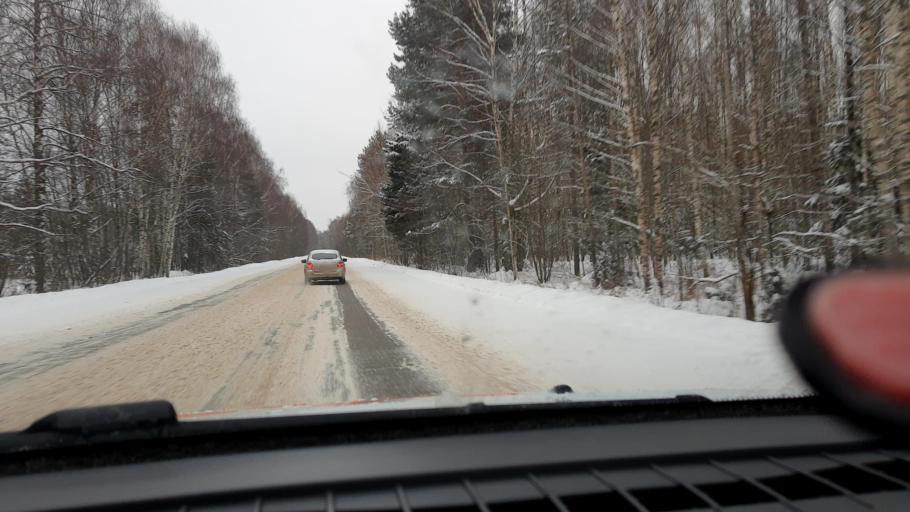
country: RU
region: Nizjnij Novgorod
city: Pamyat' Parizhskoy Kommuny
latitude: 56.2586
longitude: 44.4565
